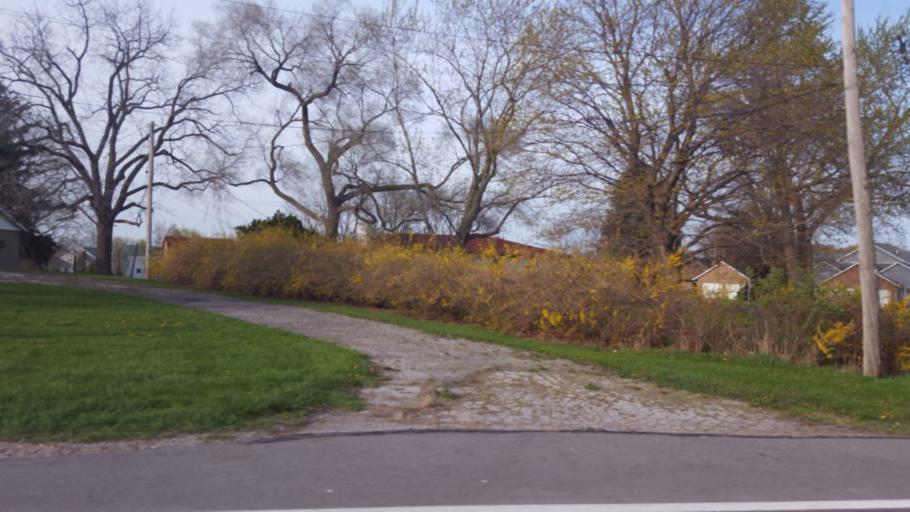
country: US
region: Ohio
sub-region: Erie County
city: Huron
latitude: 41.4115
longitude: -82.6122
